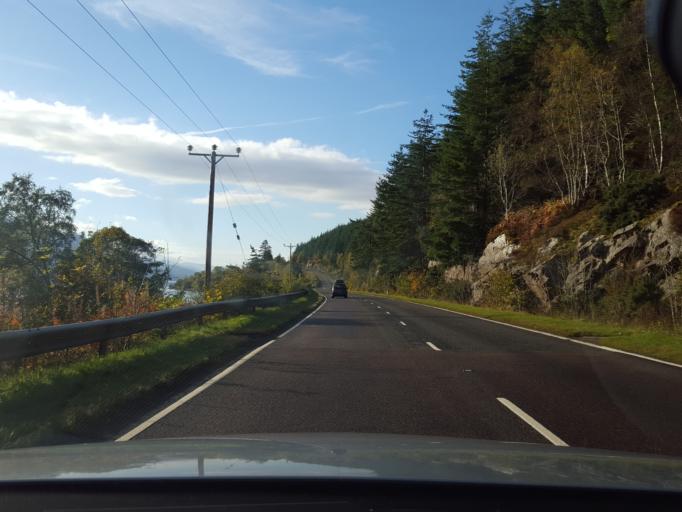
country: GB
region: Scotland
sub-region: Highland
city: Beauly
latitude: 57.2294
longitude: -4.5673
